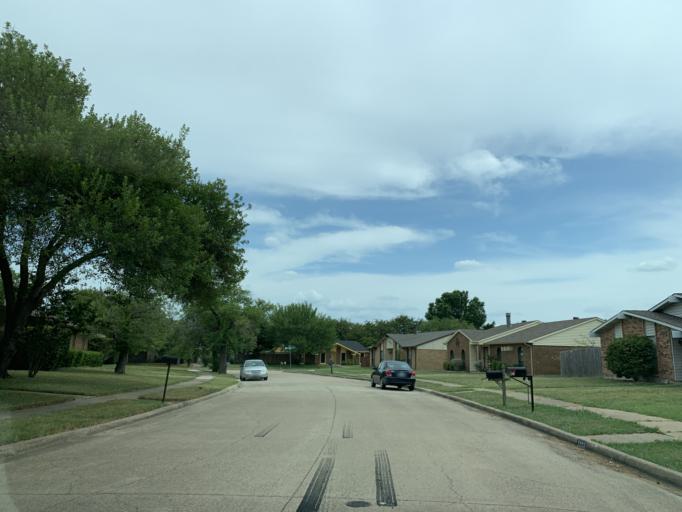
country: US
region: Texas
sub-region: Dallas County
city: Grand Prairie
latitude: 32.6533
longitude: -97.0314
